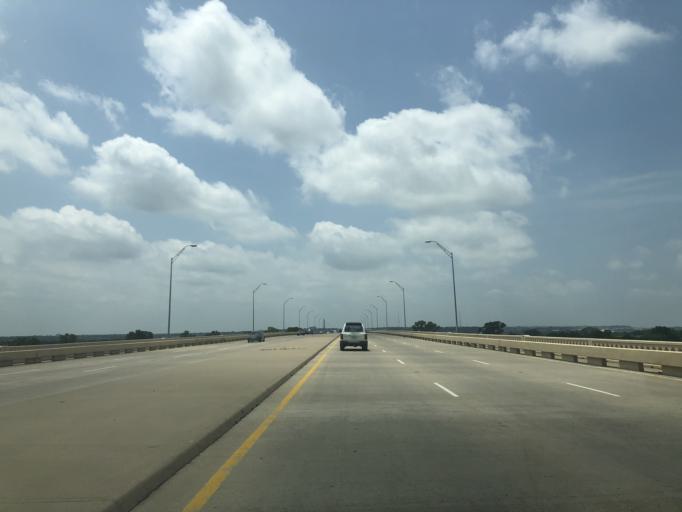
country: US
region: Texas
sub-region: Dallas County
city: Dallas
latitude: 32.8011
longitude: -96.8539
